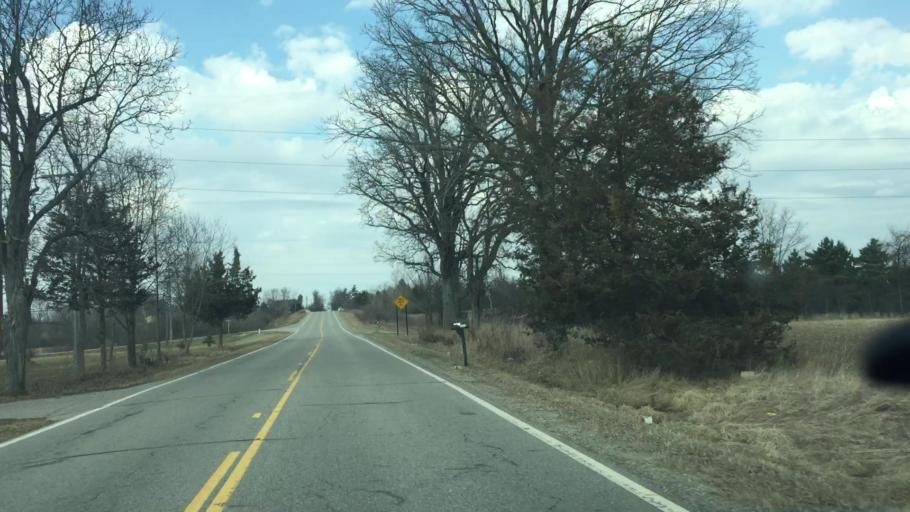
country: US
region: Michigan
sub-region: Lapeer County
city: Lapeer
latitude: 43.0098
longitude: -83.2824
